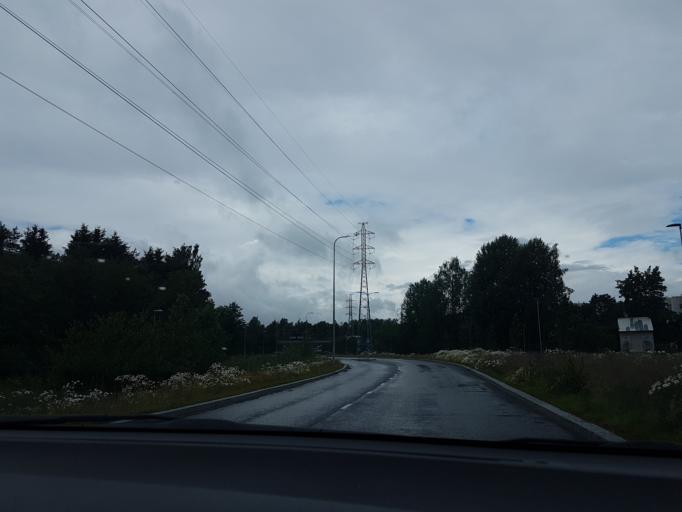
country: FI
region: Uusimaa
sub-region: Helsinki
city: Vantaa
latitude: 60.2355
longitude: 25.1098
